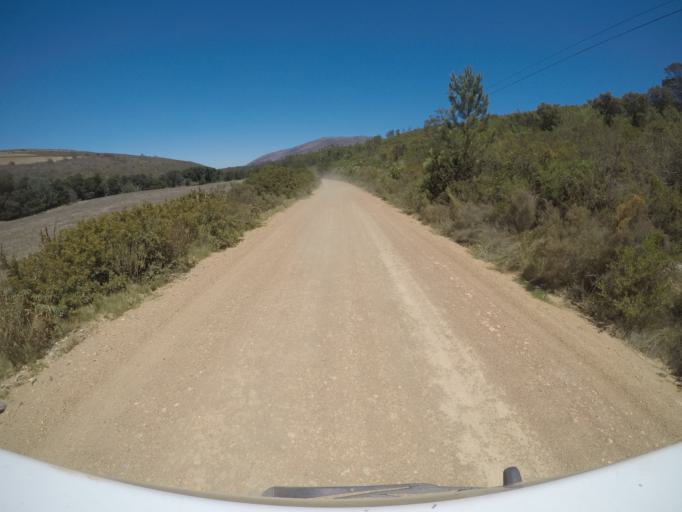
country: ZA
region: Western Cape
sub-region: Overberg District Municipality
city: Caledon
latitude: -34.1519
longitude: 19.2334
